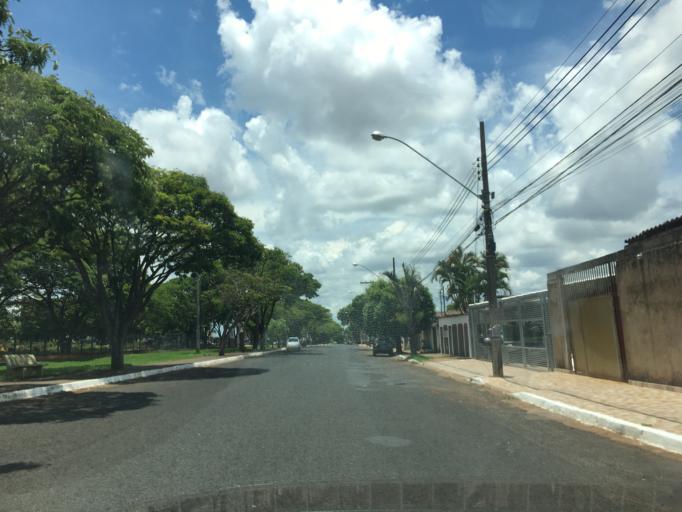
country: BR
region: Minas Gerais
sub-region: Uberlandia
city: Uberlandia
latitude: -18.9342
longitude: -48.3068
